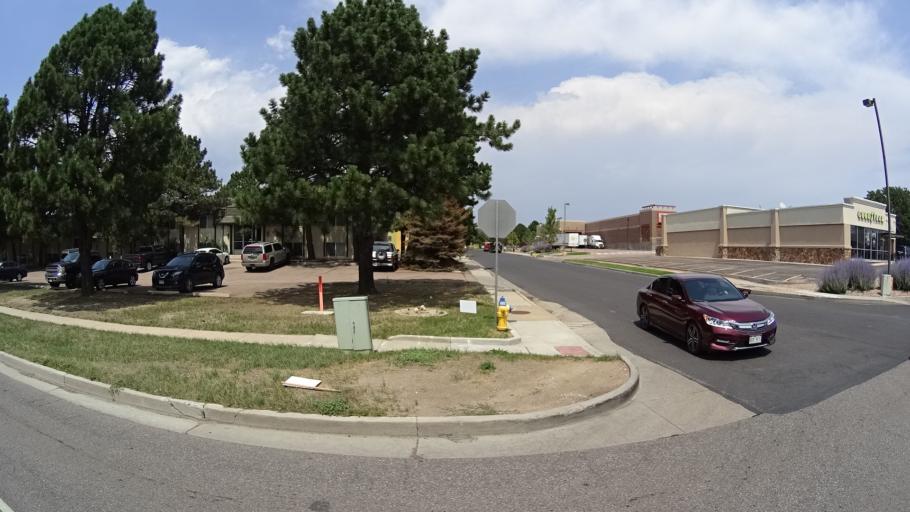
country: US
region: Colorado
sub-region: El Paso County
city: Cimarron Hills
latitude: 38.8908
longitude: -104.7617
